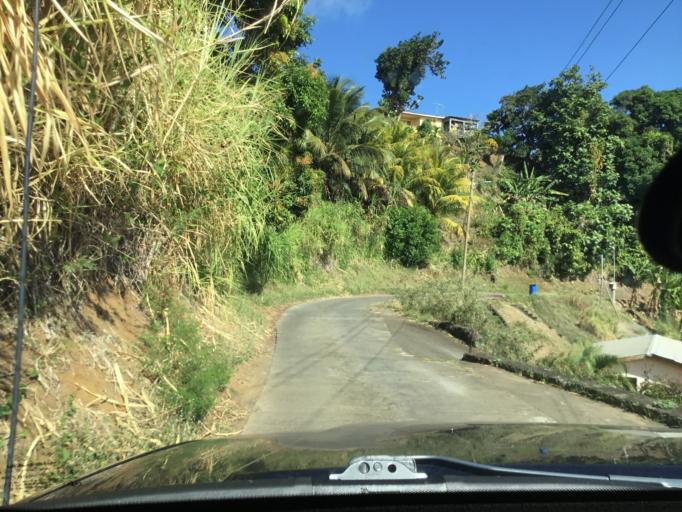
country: VC
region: Charlotte
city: Biabou
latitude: 13.1604
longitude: -61.1627
